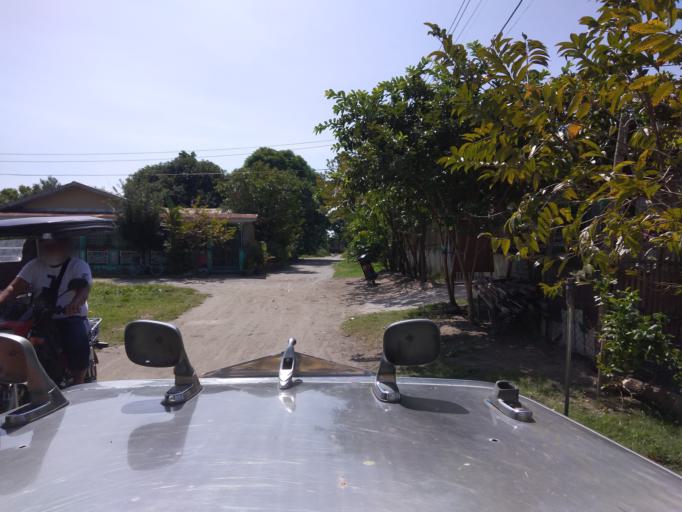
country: PH
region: Central Luzon
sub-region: Province of Pampanga
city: San Juan
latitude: 15.0046
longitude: 120.6712
